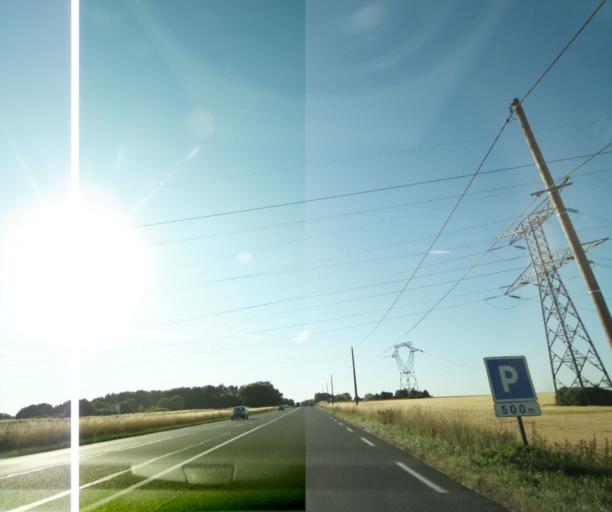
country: FR
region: Ile-de-France
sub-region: Departement de Seine-et-Marne
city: Vernou-la-Celle-sur-Seine
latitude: 48.3621
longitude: 2.8589
